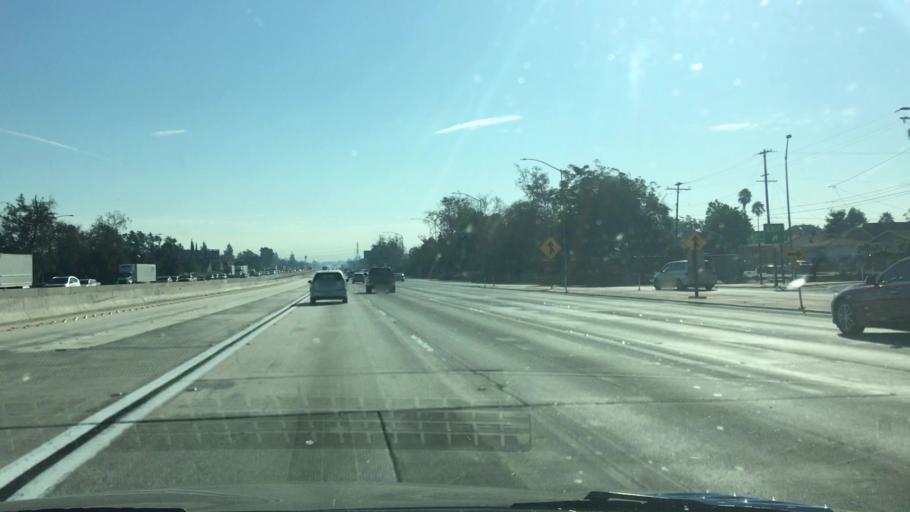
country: US
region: California
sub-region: Los Angeles County
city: South San Gabriel
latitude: 34.0718
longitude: -118.0994
